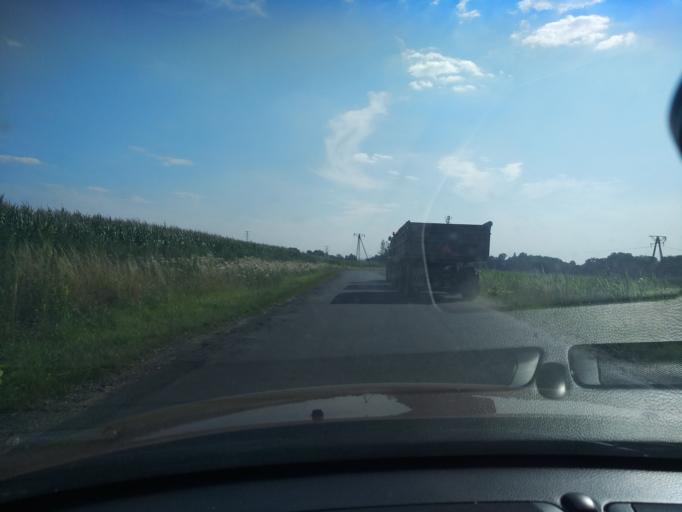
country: PL
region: Lower Silesian Voivodeship
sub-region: Powiat zgorzelecki
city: Sulikow
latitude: 51.0843
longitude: 15.1287
